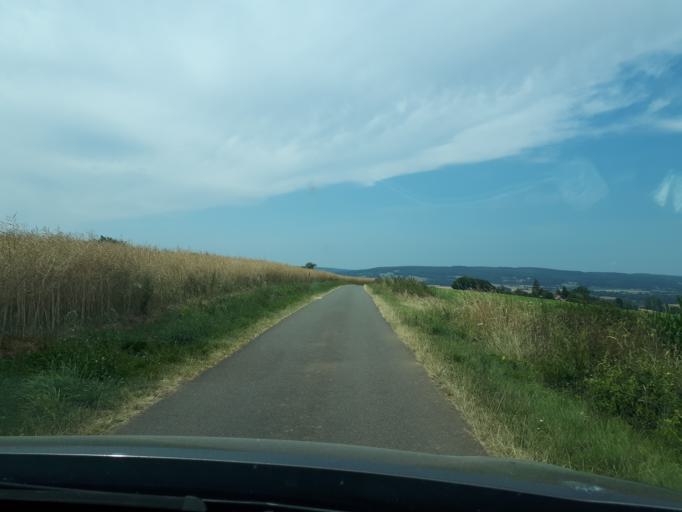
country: FR
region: Centre
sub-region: Departement du Cher
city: Sancerre
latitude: 47.3117
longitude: 2.7370
